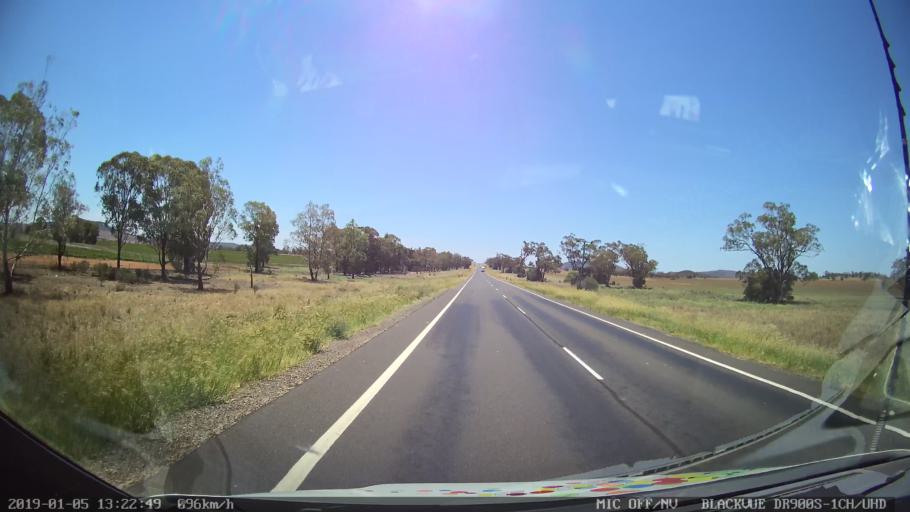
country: AU
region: New South Wales
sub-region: Gunnedah
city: Gunnedah
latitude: -31.0831
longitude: 149.9669
